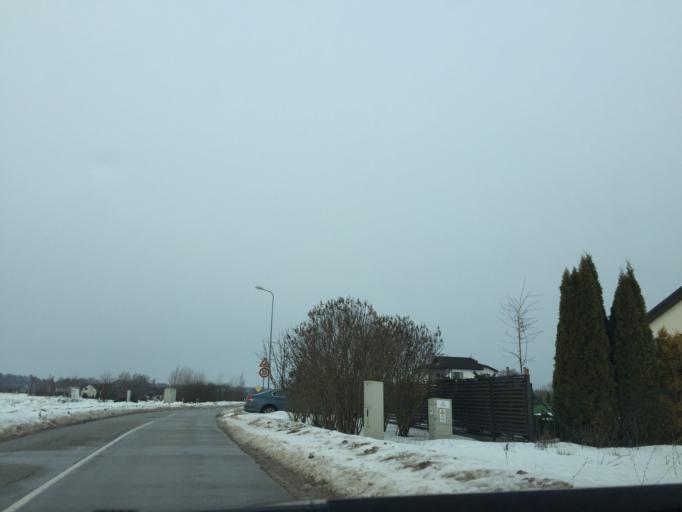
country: LV
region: Ikskile
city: Ikskile
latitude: 56.8377
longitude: 24.4767
